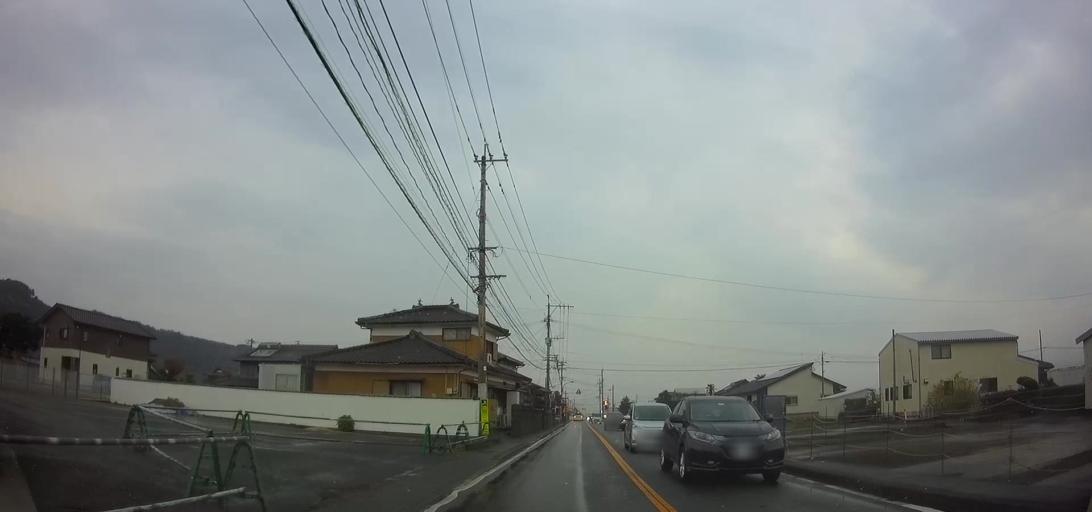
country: JP
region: Nagasaki
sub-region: Isahaya-shi
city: Isahaya
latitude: 32.8347
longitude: 130.1114
